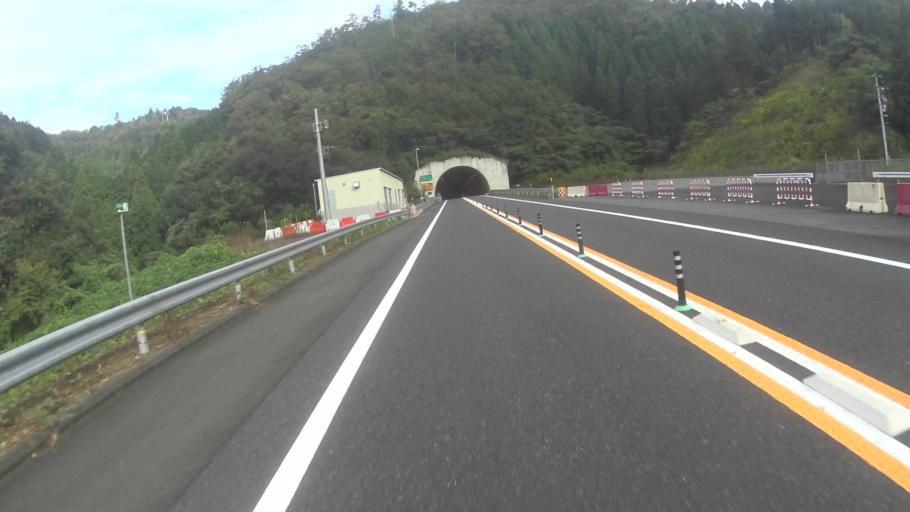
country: JP
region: Kyoto
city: Ayabe
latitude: 35.3206
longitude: 135.3171
